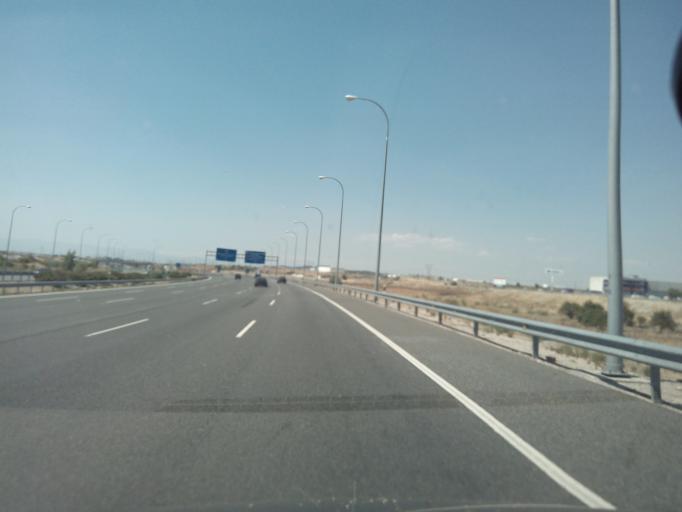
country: ES
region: Madrid
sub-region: Provincia de Madrid
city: San Fernando de Henares
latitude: 40.4277
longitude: -3.4994
